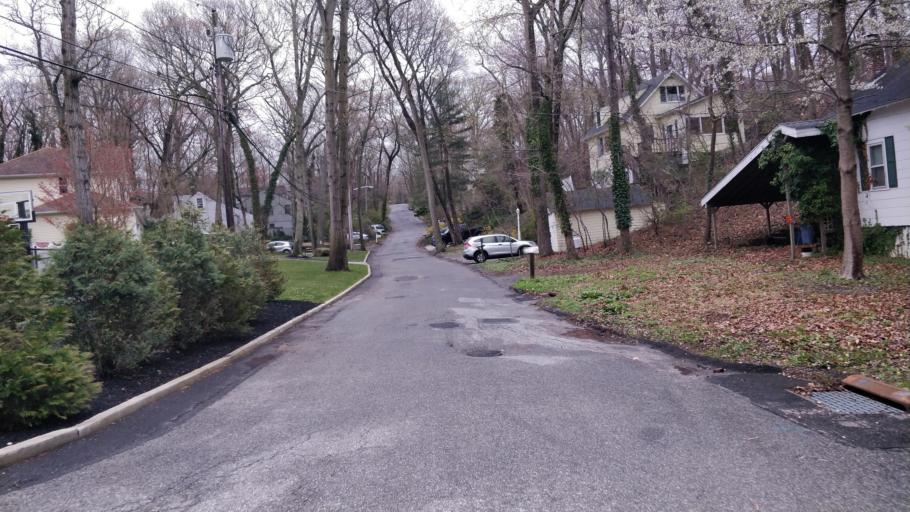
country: US
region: New York
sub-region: Suffolk County
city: Port Jefferson
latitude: 40.9530
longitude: -73.0858
